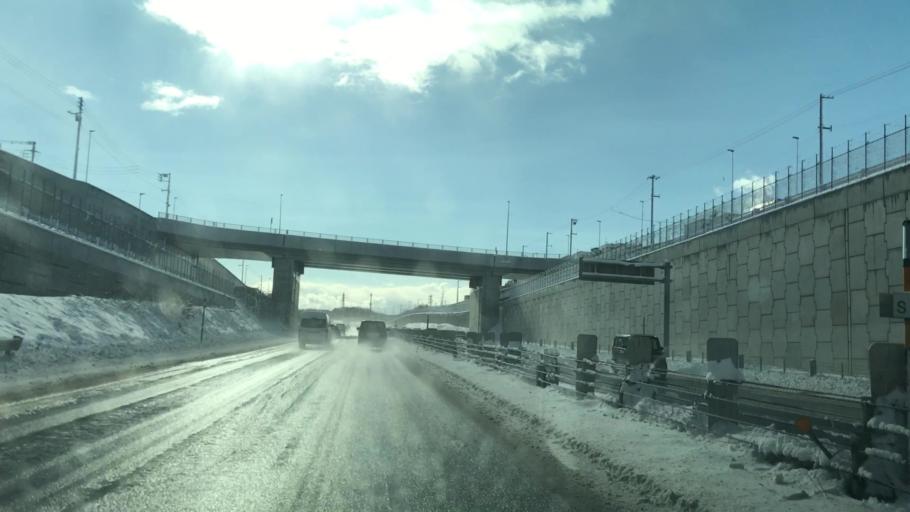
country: JP
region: Hokkaido
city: Kitahiroshima
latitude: 42.9938
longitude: 141.4691
